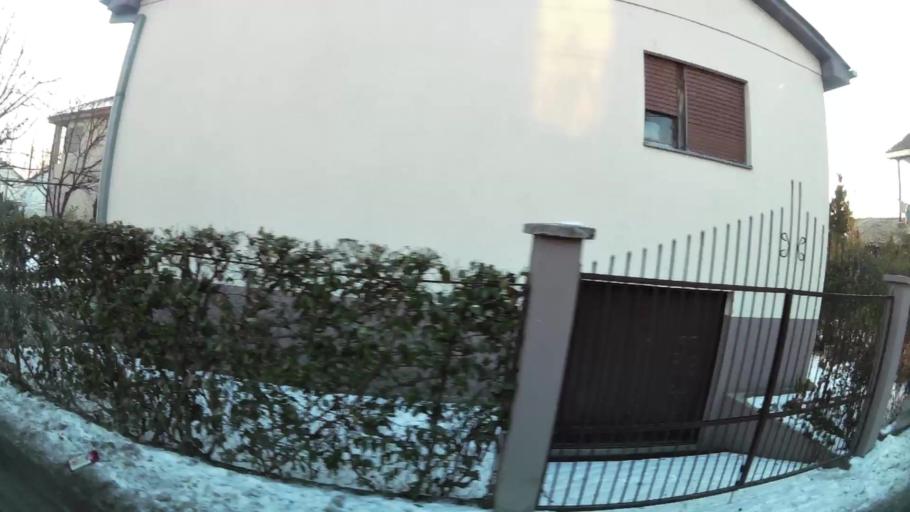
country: MK
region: Kisela Voda
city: Kisela Voda
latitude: 41.9777
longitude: 21.4939
